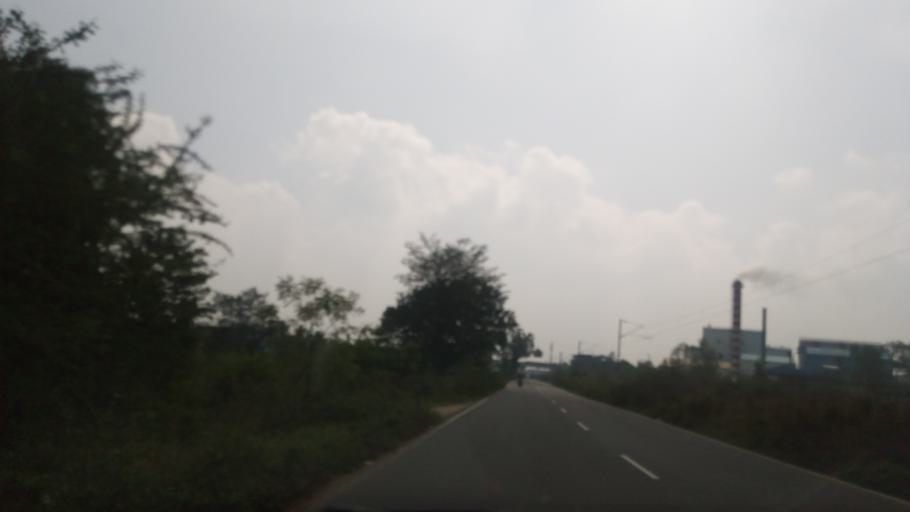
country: IN
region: Tamil Nadu
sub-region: Kancheepuram
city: Kanchipuram
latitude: 12.8791
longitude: 79.6895
